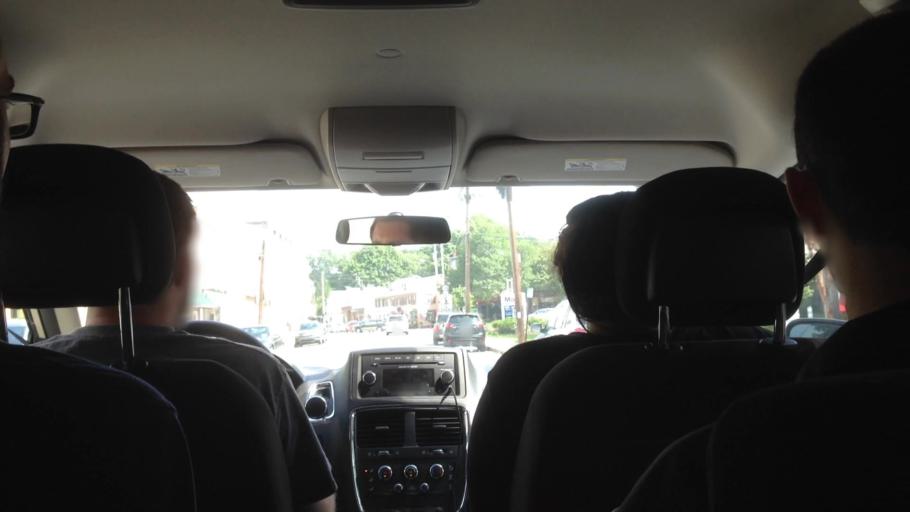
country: US
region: New York
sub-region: Dutchess County
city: Red Hook
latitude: 41.9956
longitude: -73.8772
